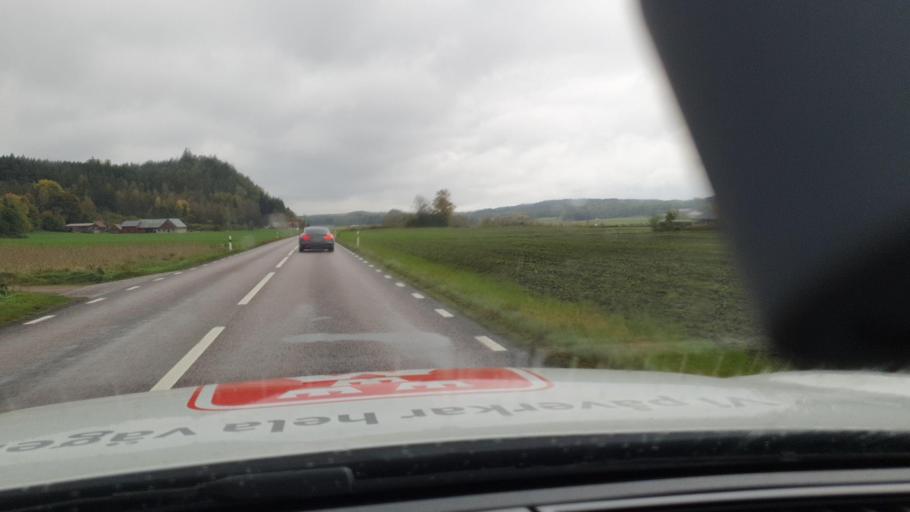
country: SE
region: Halland
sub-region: Falkenbergs Kommun
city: Falkenberg
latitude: 57.0544
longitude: 12.6156
